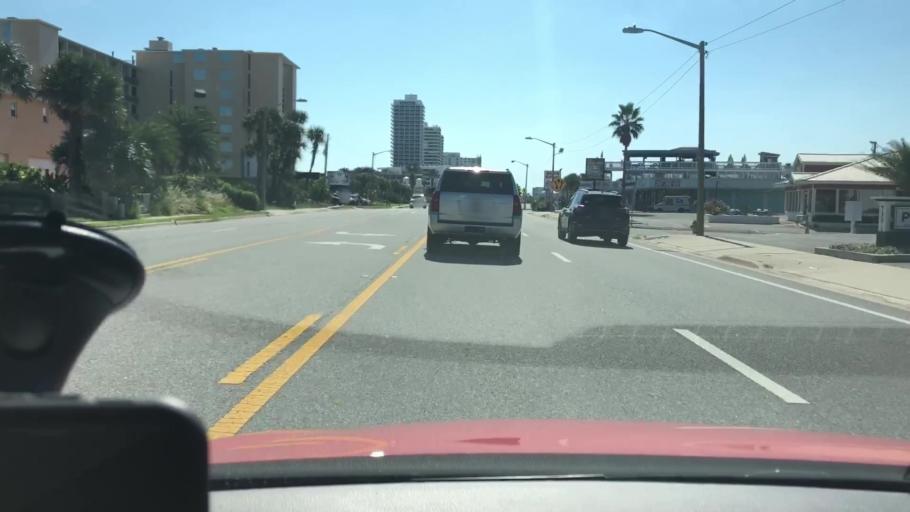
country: US
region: Florida
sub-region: Volusia County
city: Ormond Beach
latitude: 29.2733
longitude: -81.0307
